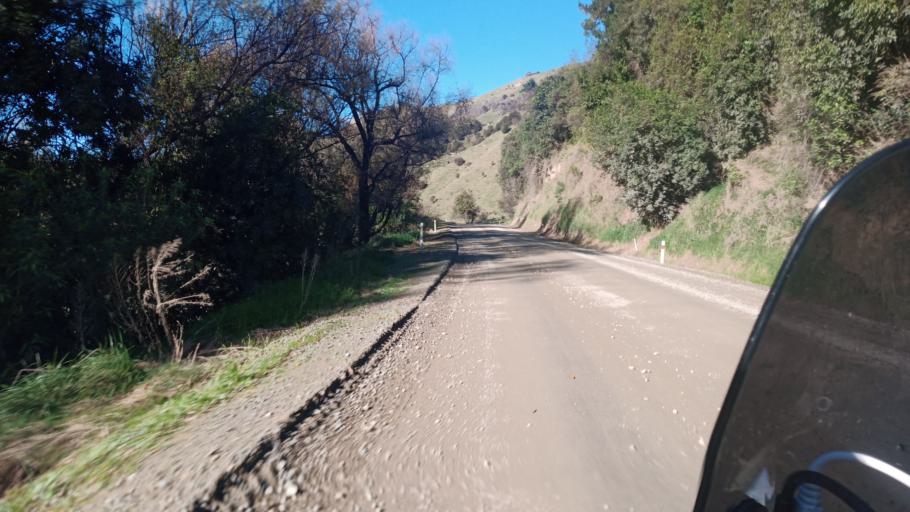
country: NZ
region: Hawke's Bay
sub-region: Wairoa District
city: Wairoa
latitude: -38.8469
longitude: 177.1659
